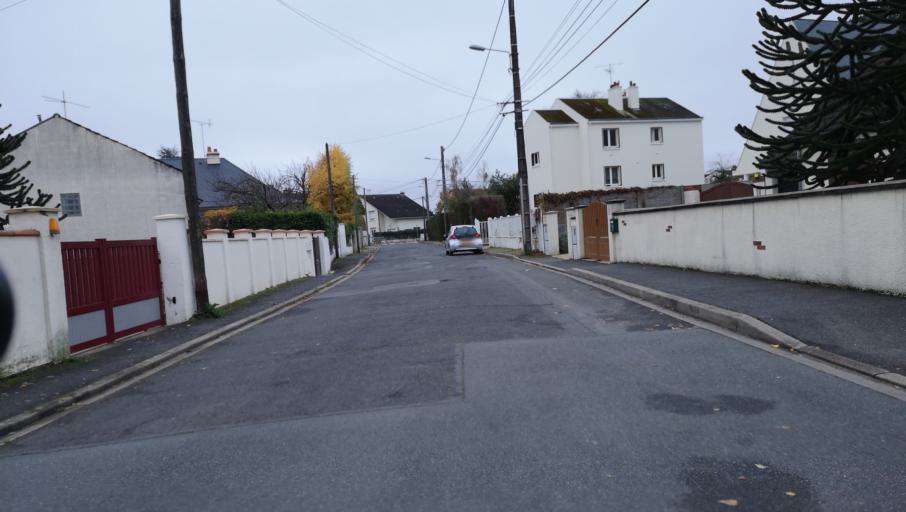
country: FR
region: Centre
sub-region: Departement du Loiret
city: Fleury-les-Aubrais
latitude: 47.9207
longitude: 1.9318
